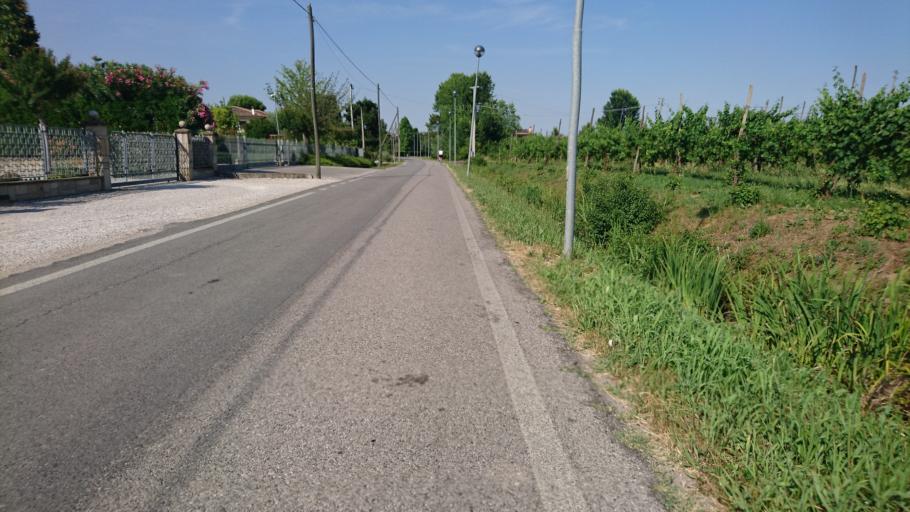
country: IT
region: Veneto
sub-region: Provincia di Padova
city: Montegrotto Terme
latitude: 45.3360
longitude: 11.8027
